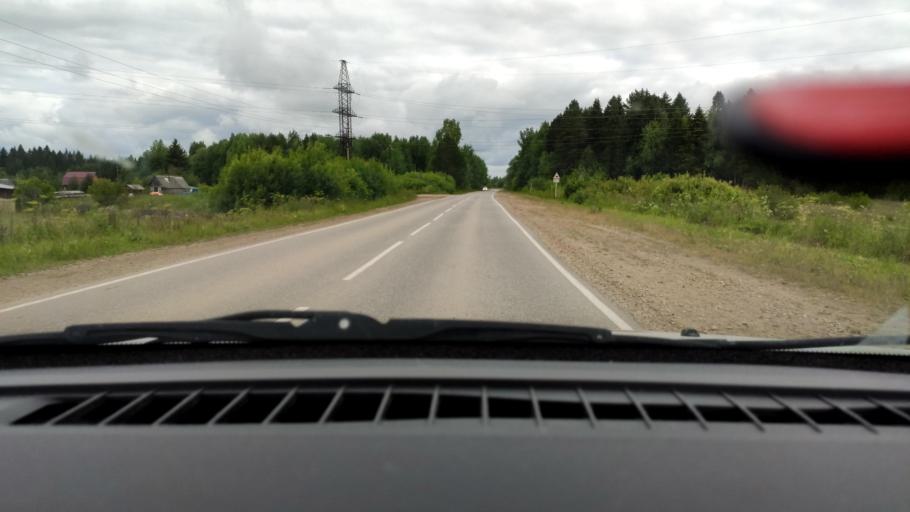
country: RU
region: Perm
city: Chaykovskaya
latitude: 58.0836
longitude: 55.6149
